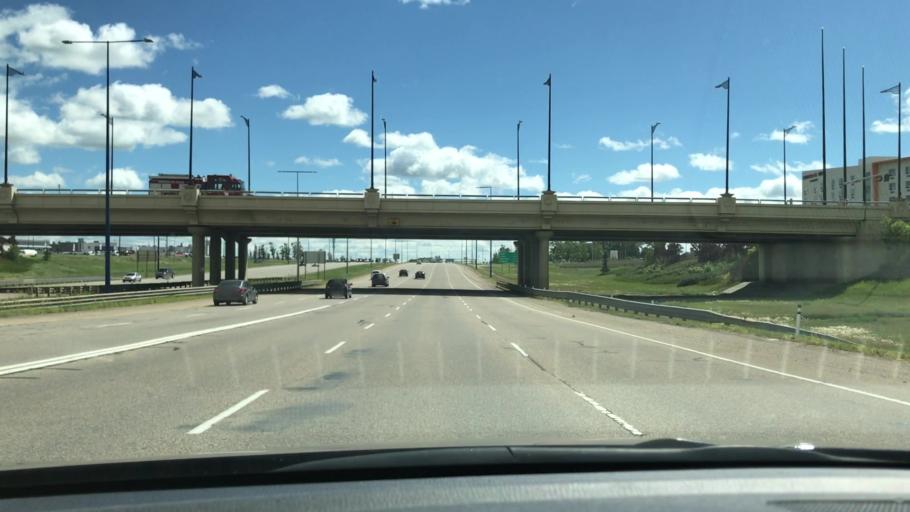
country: CA
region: Alberta
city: Beaumont
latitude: 53.4256
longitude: -113.4939
